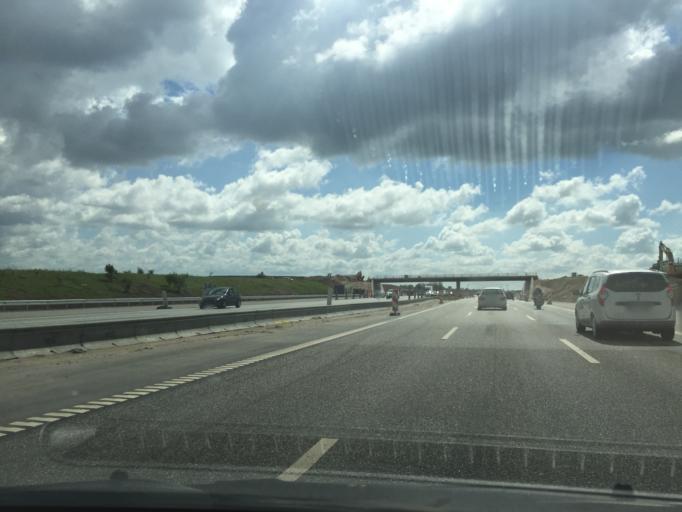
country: DK
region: Zealand
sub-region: Solrod Kommune
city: Solrod
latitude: 55.5072
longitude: 12.1771
